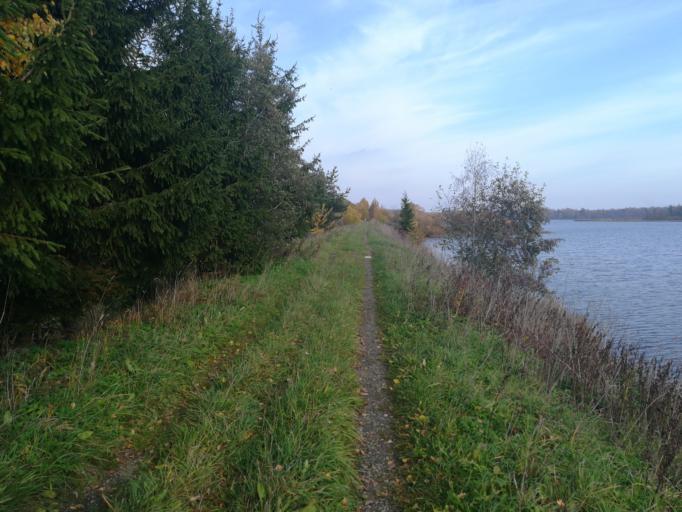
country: RU
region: Leningrad
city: Sista-Palkino
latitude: 59.5909
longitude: 28.8263
